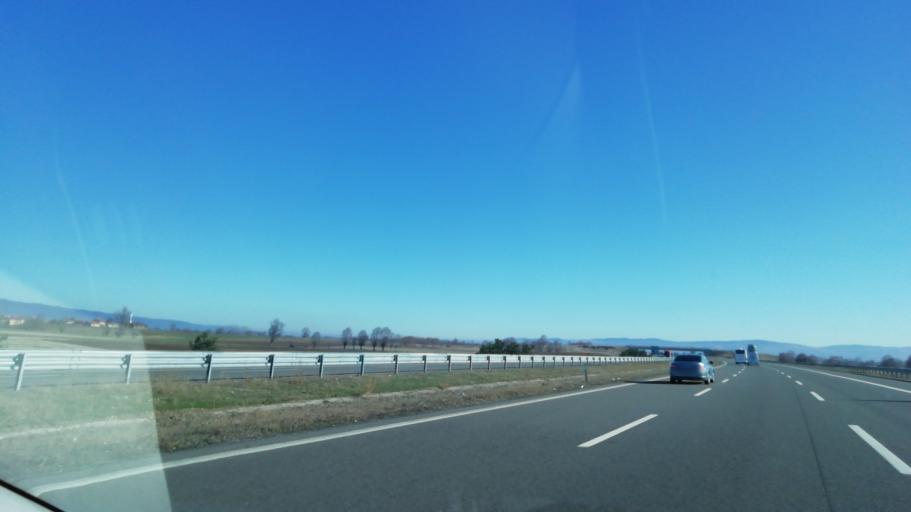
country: TR
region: Bolu
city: Dortdivan
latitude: 40.7398
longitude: 32.1339
